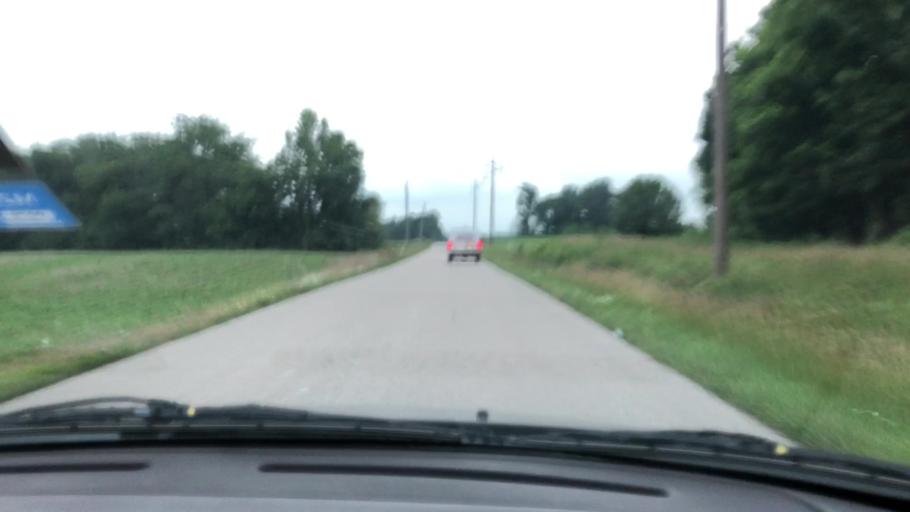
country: US
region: Indiana
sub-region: Greene County
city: Linton
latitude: 38.9819
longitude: -87.2981
